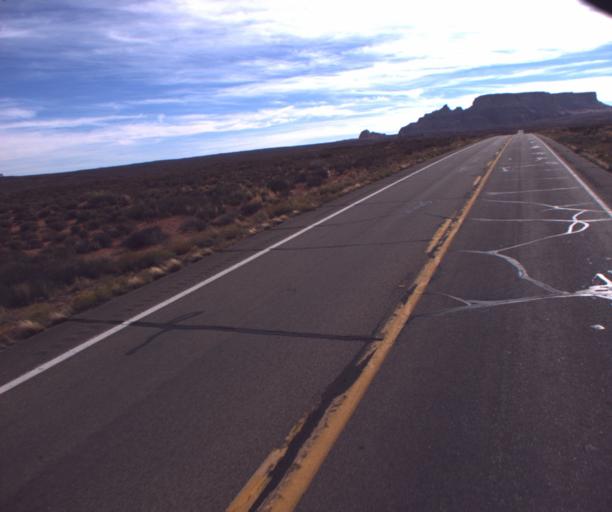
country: US
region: Arizona
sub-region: Coconino County
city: LeChee
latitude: 36.8861
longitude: -111.3604
